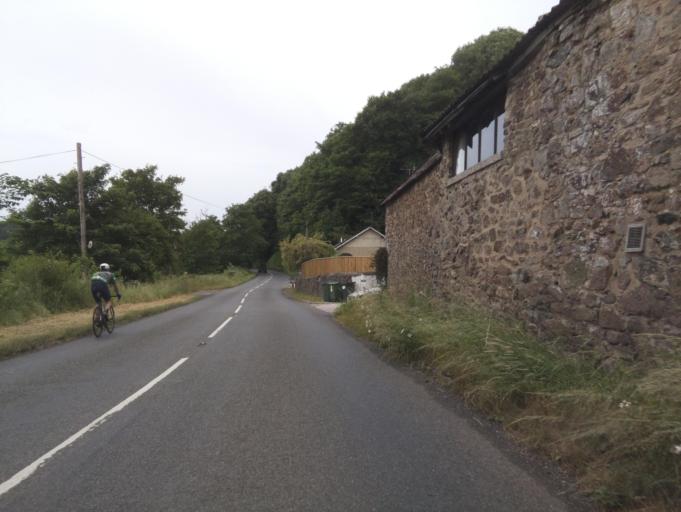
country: GB
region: England
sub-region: Devon
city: Chudleigh
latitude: 50.6011
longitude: -3.6196
